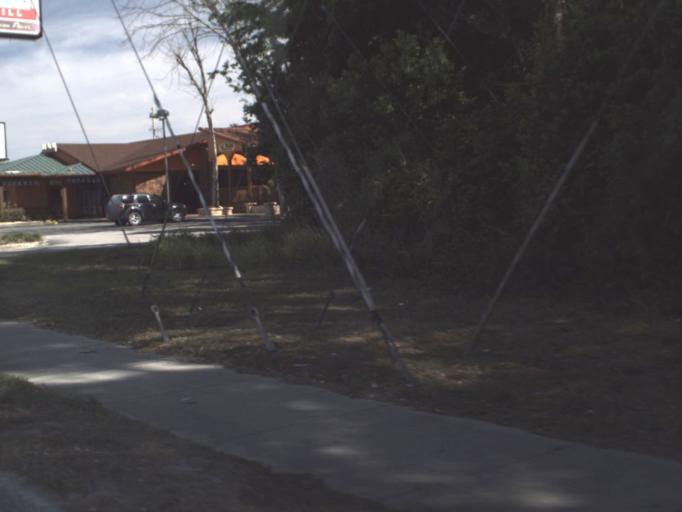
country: US
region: Florida
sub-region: Lake County
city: Leesburg
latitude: 28.8324
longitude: -81.8881
